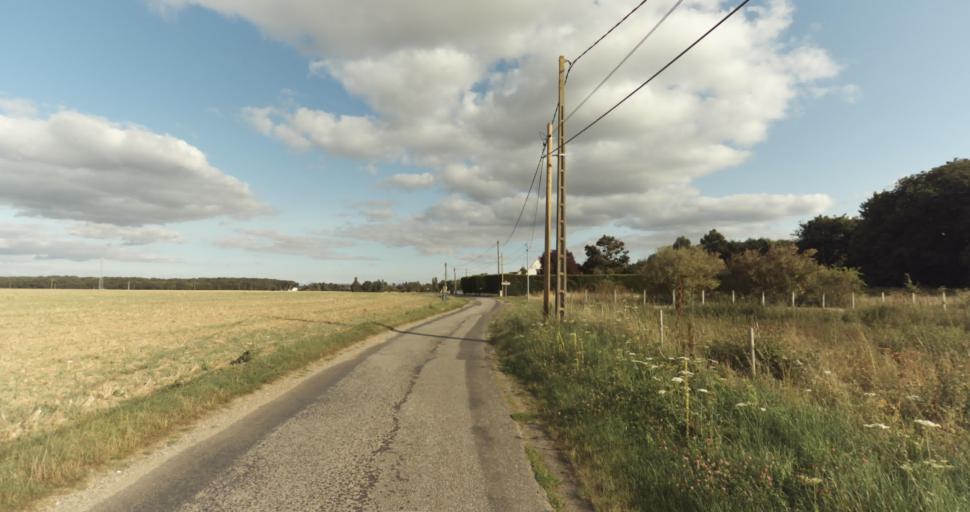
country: FR
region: Haute-Normandie
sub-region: Departement de l'Eure
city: La Couture-Boussey
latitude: 48.9011
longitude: 1.3484
